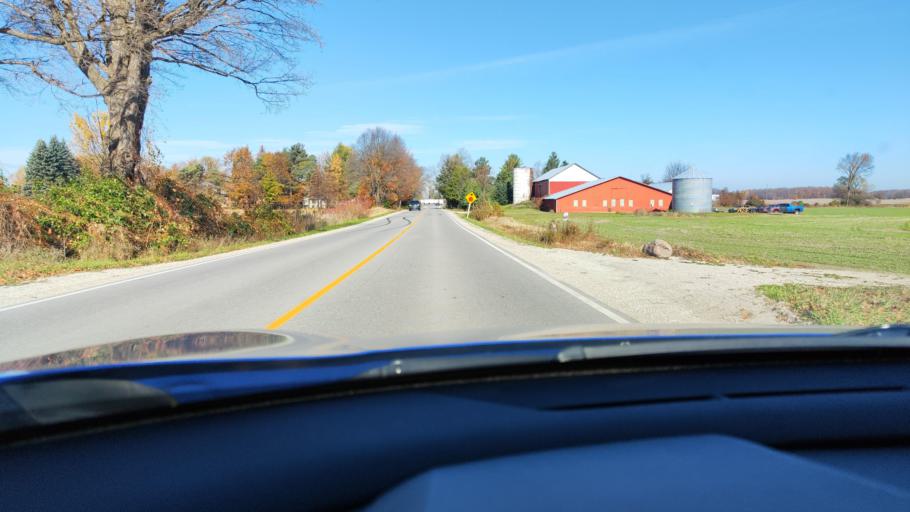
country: CA
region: Ontario
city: Wasaga Beach
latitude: 44.4196
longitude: -80.0622
